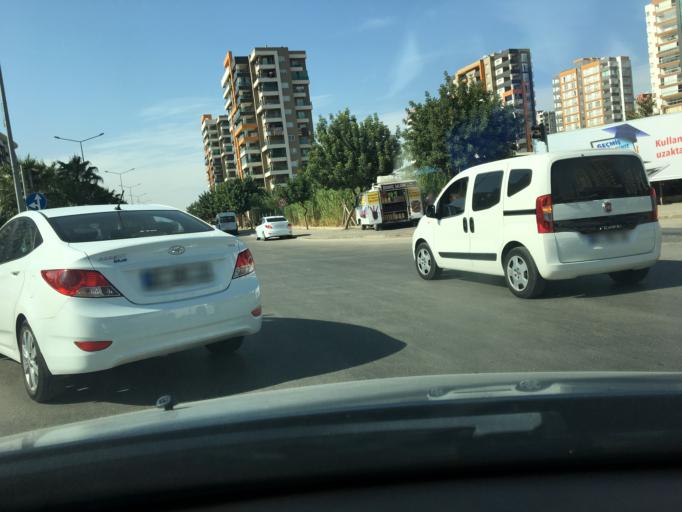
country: TR
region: Adana
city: Seyhan
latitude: 37.0224
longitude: 35.2583
